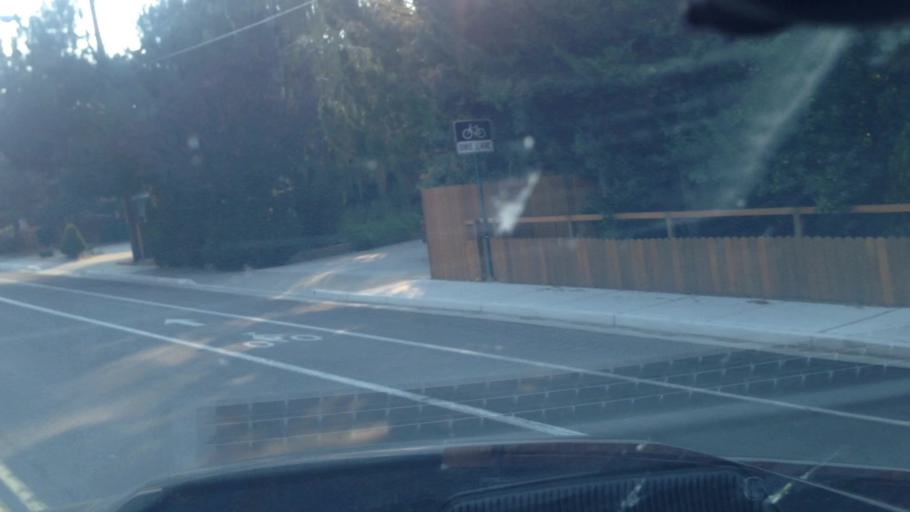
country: US
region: Nevada
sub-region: Washoe County
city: Reno
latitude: 39.5084
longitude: -119.8415
